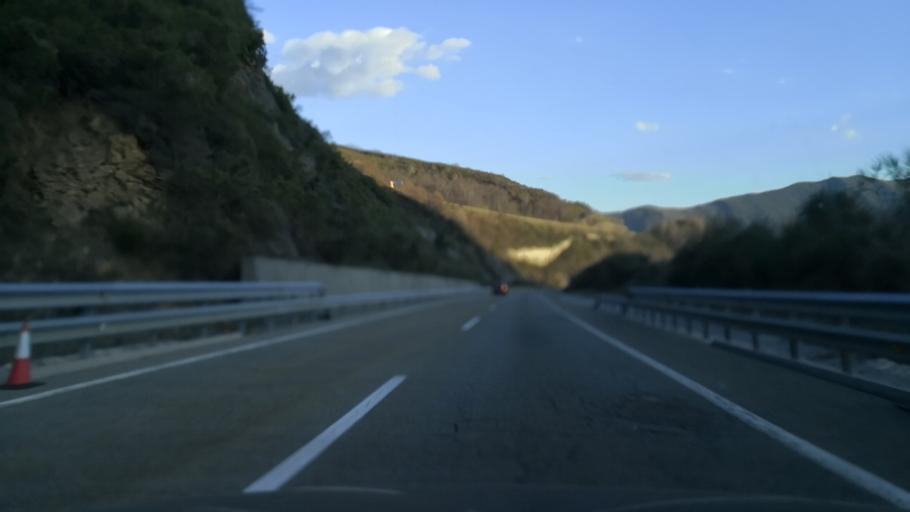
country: ES
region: Castille and Leon
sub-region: Provincia de Leon
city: Vega de Valcarce
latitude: 42.6889
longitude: -6.9902
